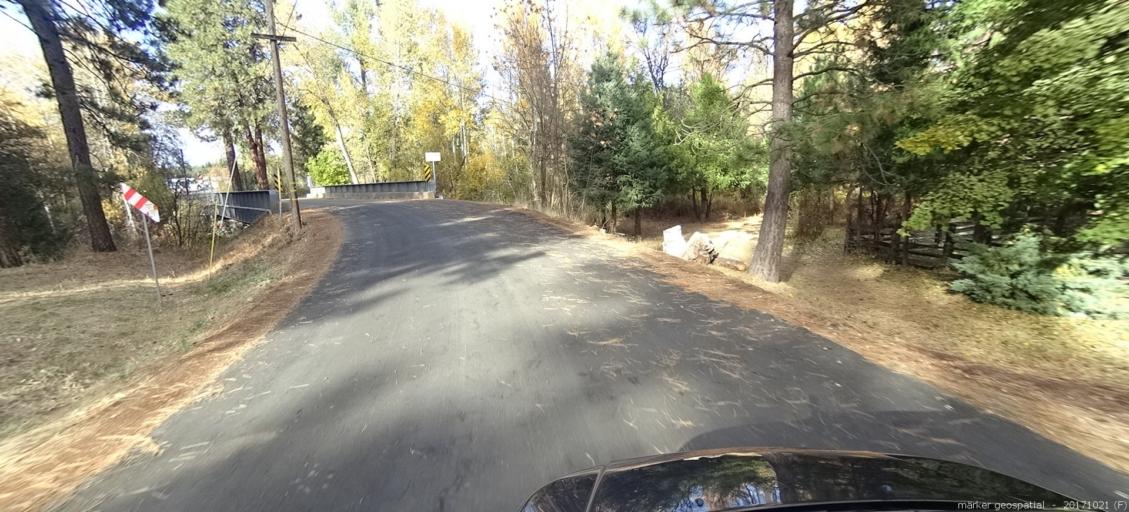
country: US
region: California
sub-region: Shasta County
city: Burney
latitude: 40.8709
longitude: -121.6973
